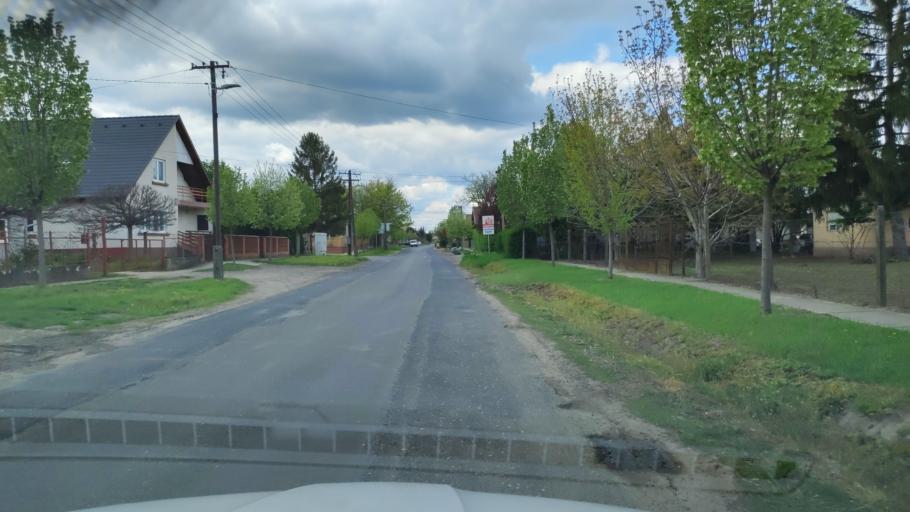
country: HU
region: Pest
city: Cegledbercel
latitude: 47.2105
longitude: 19.7292
